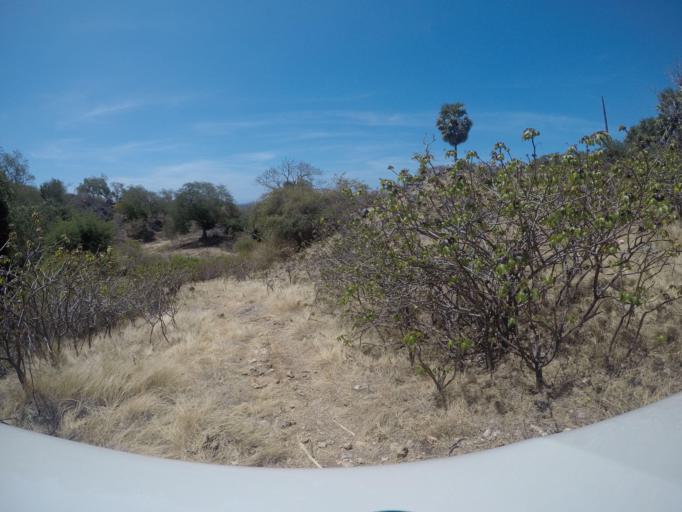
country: TL
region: Baucau
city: Baucau
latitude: -8.4327
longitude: 126.4422
